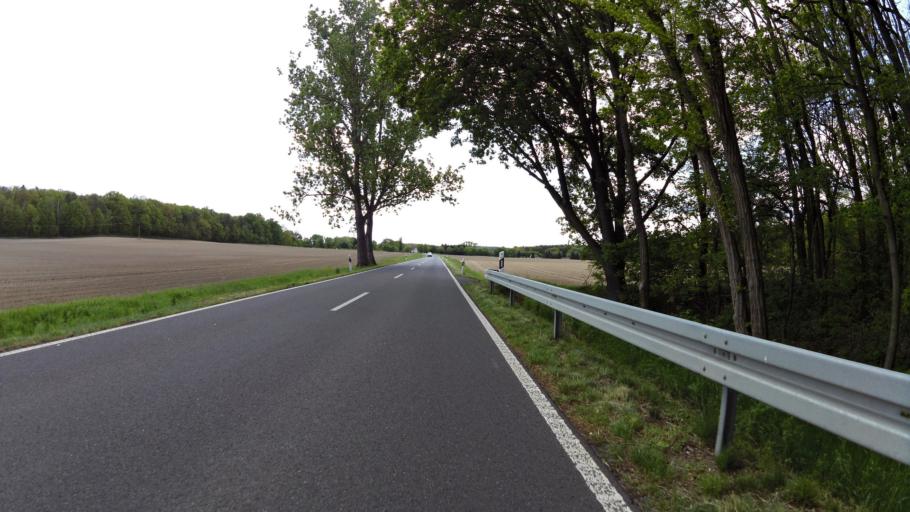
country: DE
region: Brandenburg
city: Rietz Neuendorf
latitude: 52.2484
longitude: 14.1229
